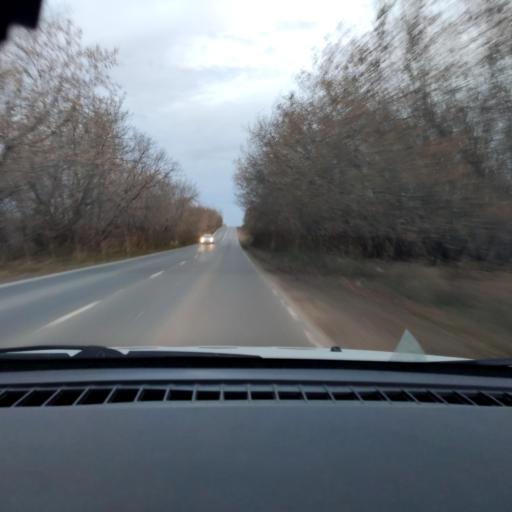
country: RU
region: Perm
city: Gamovo
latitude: 57.9078
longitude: 56.1656
